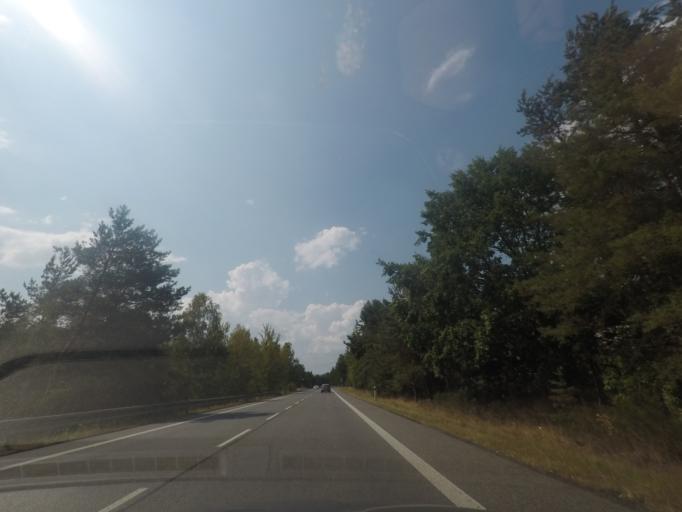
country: CZ
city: Cvikov
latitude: 50.7749
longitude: 14.6568
